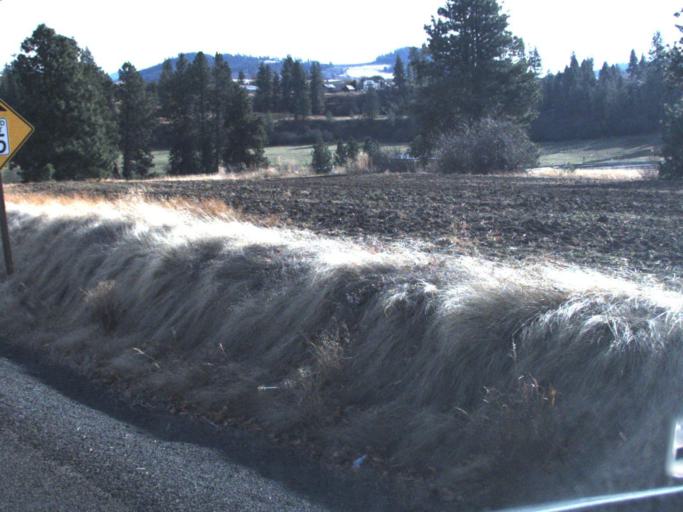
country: US
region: Idaho
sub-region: Latah County
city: Moscow
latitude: 46.9167
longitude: -117.0868
